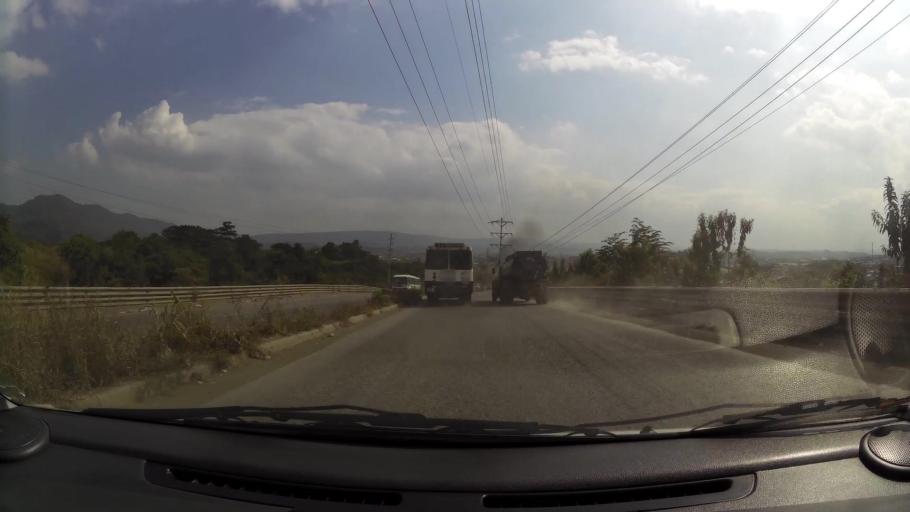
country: EC
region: Guayas
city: Santa Lucia
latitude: -2.1203
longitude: -79.9758
